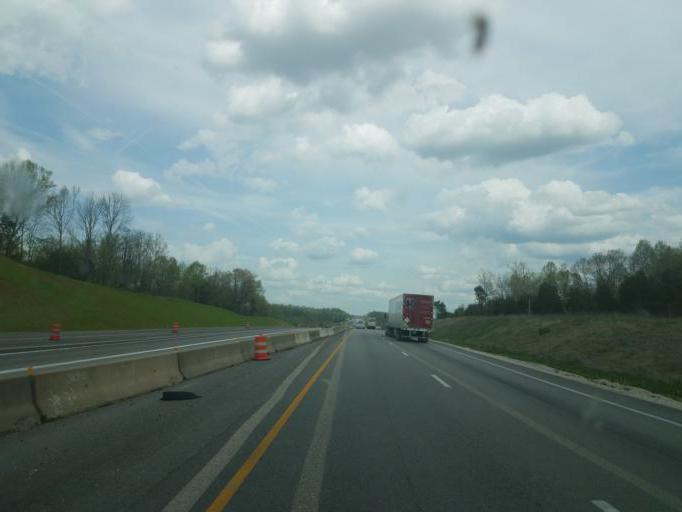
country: US
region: Kentucky
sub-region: Hart County
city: Munfordville
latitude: 37.3692
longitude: -85.8919
